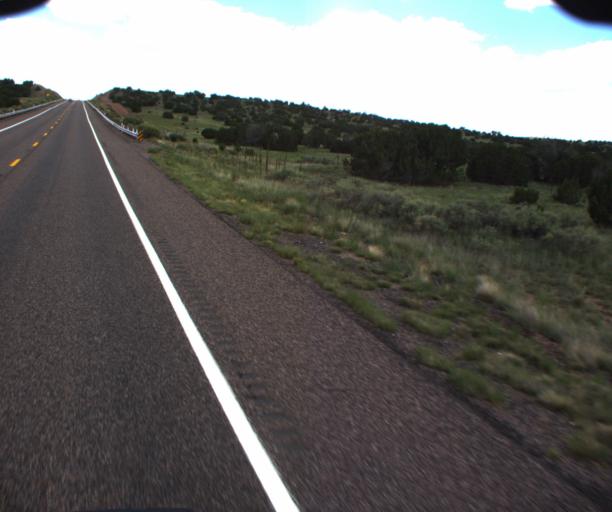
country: US
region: Arizona
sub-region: Apache County
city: Springerville
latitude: 34.1541
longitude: -109.1412
